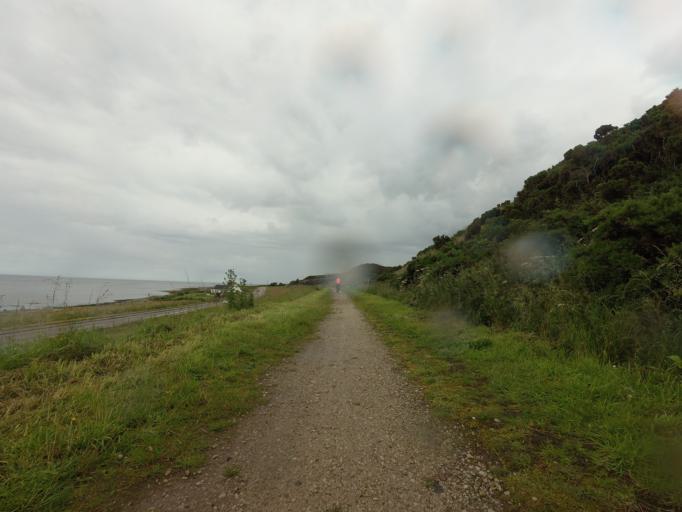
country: GB
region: Scotland
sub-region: Moray
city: Buckie
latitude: 57.6679
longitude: -2.9994
